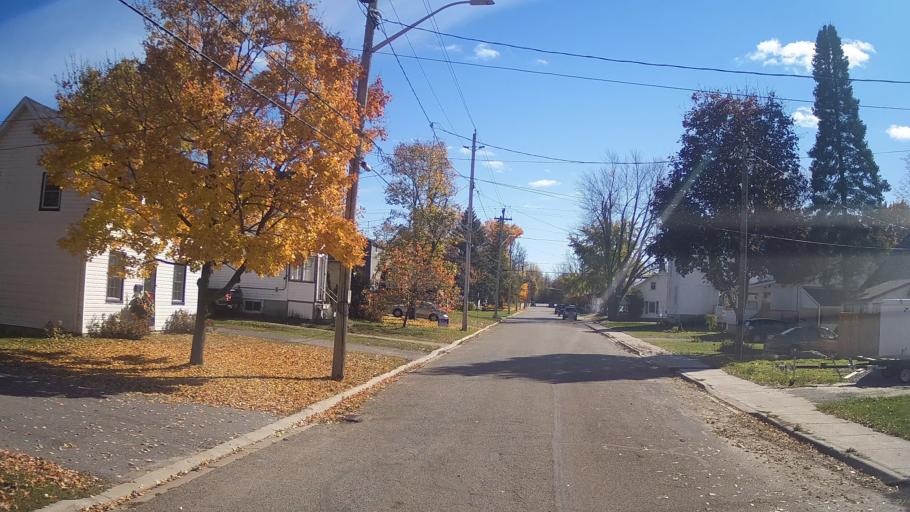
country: CA
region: Ontario
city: Perth
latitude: 44.8966
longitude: -76.2407
